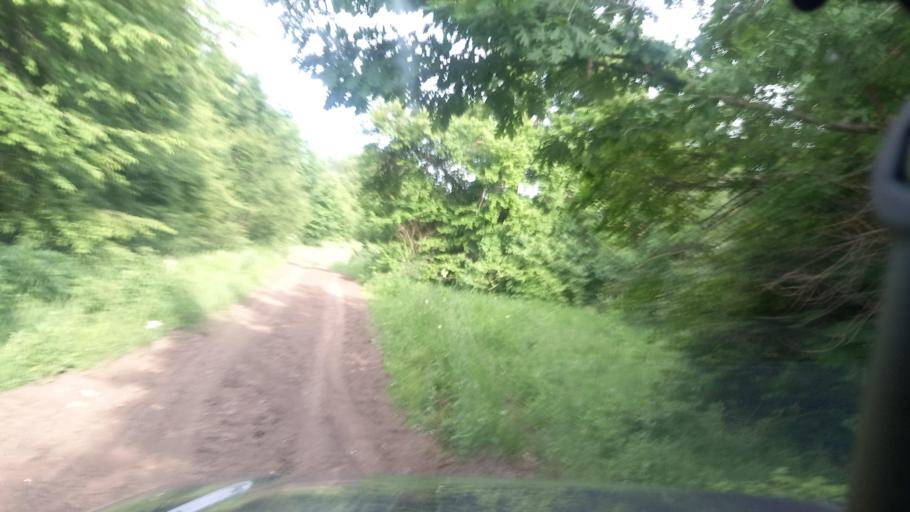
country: RU
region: Karachayevo-Cherkesiya
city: Kurdzhinovo
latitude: 44.1253
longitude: 41.0805
